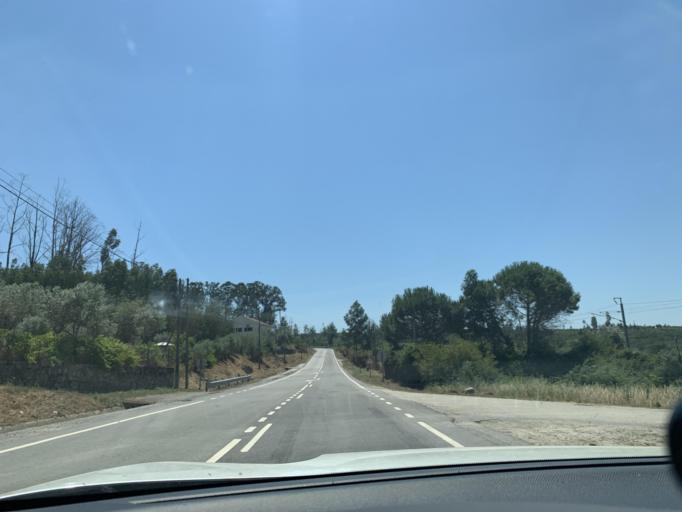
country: PT
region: Viseu
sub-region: Mangualde
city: Mangualde
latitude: 40.5798
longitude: -7.7465
